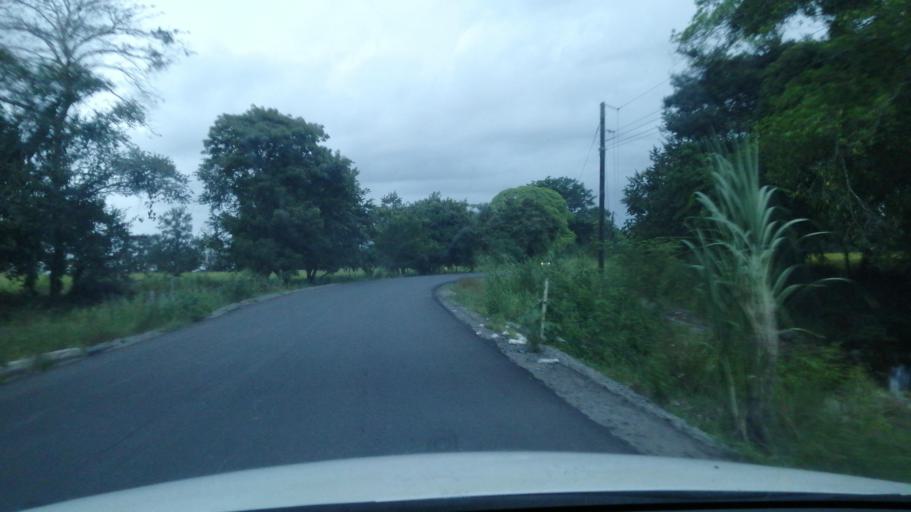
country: PA
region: Chiriqui
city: Alanje
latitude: 8.3963
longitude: -82.4906
